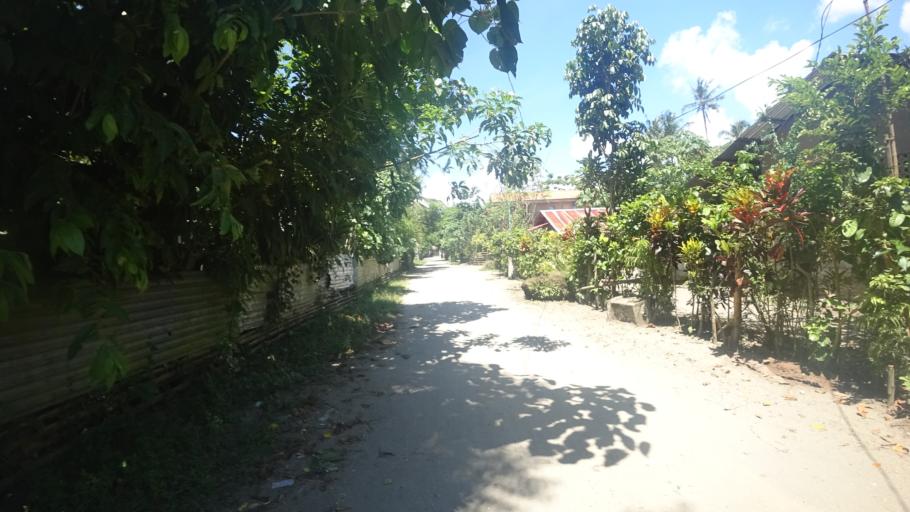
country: PH
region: Eastern Visayas
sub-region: Province of Leyte
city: Mayorga
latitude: 10.8913
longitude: 125.0090
